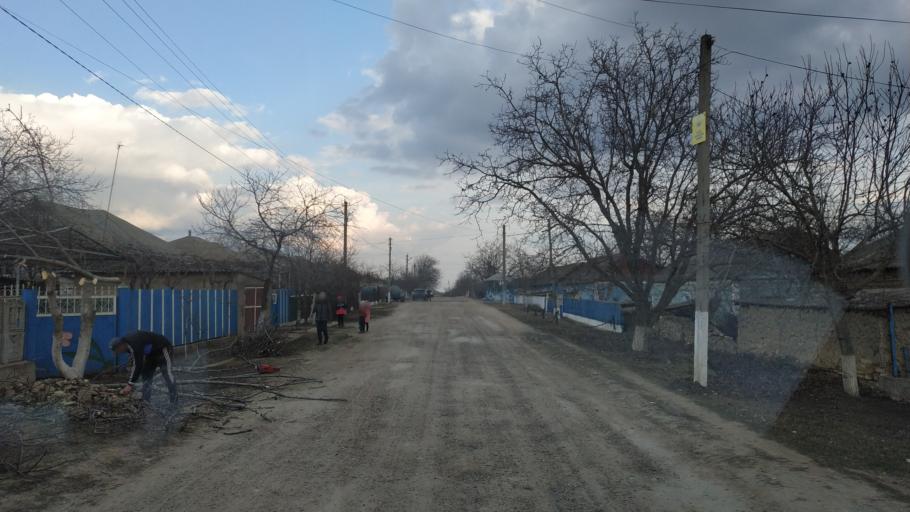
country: MD
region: Telenesti
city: Grigoriopol
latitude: 47.0093
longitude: 29.3001
